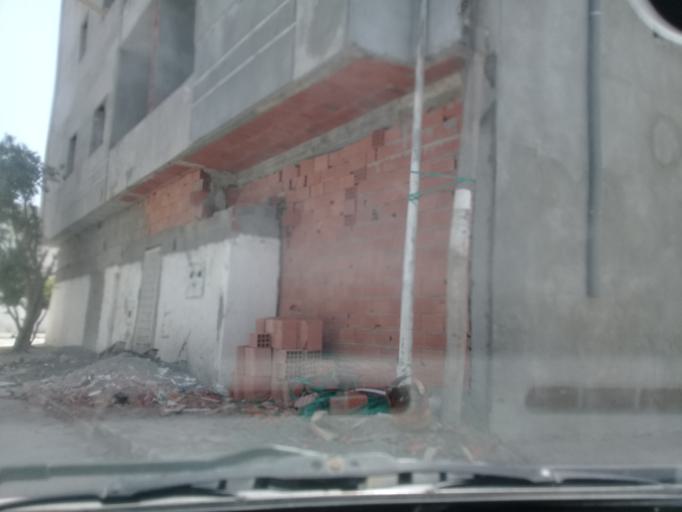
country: TN
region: Ariana
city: Ariana
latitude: 36.8343
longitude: 10.1998
